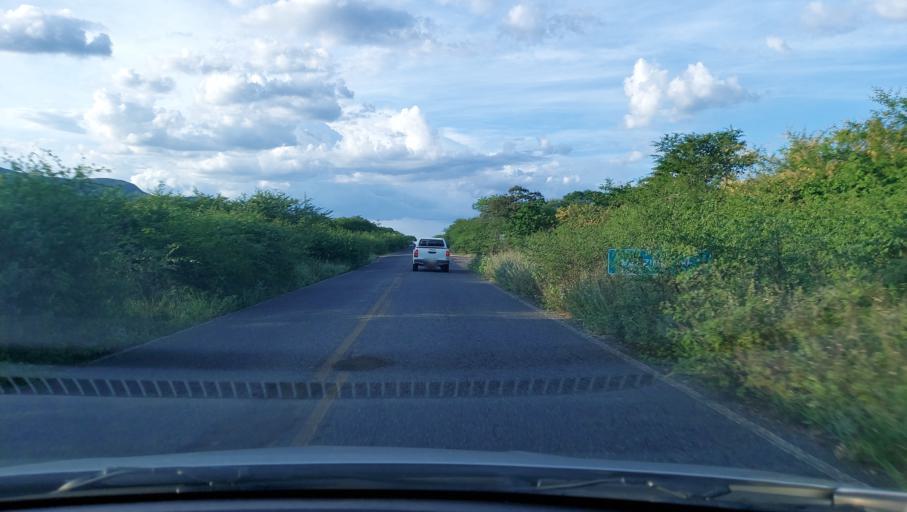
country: BR
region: Bahia
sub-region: Oliveira Dos Brejinhos
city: Beira Rio
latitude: -12.1909
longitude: -42.5379
